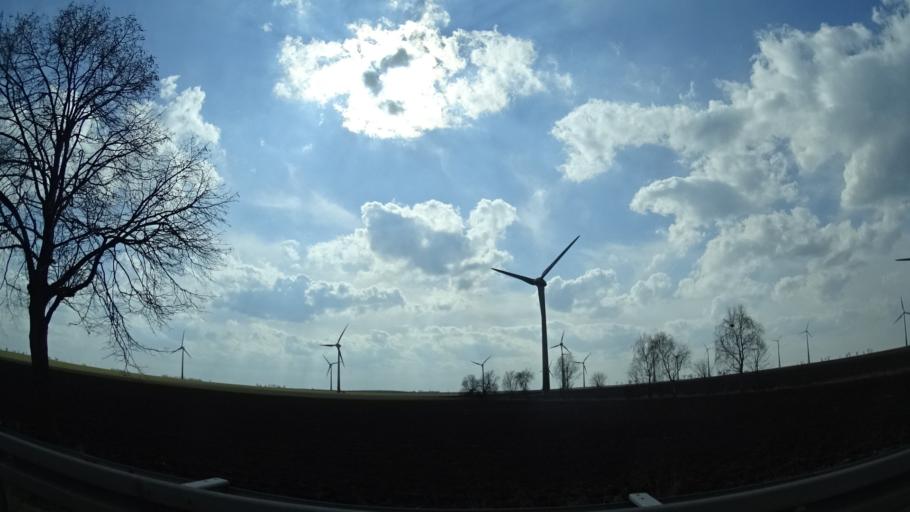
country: DE
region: Saxony-Anhalt
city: Stossen
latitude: 51.1004
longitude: 11.9386
